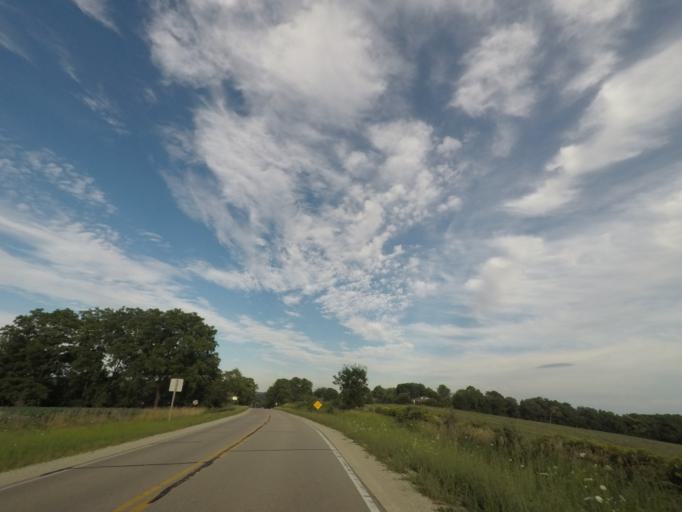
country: US
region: Wisconsin
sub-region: Green County
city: New Glarus
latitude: 42.8144
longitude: -89.6502
